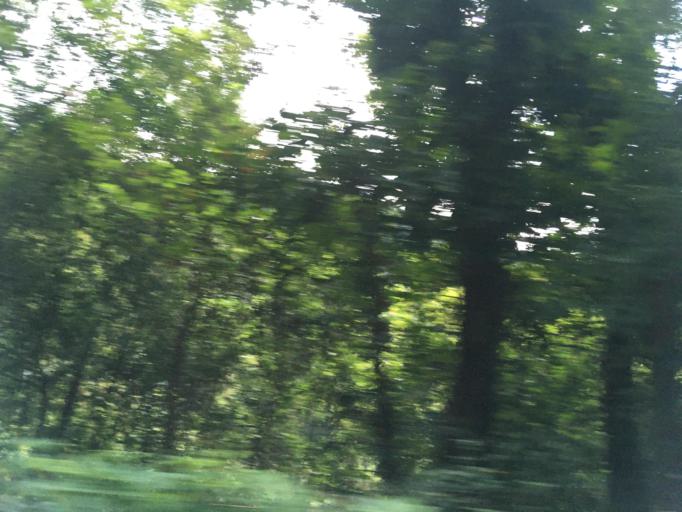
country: TW
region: Taipei
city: Taipei
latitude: 24.9491
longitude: 121.5576
